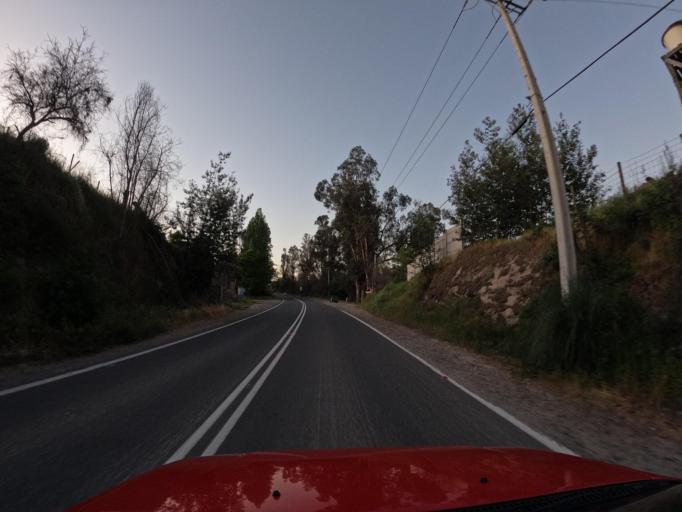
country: CL
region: O'Higgins
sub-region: Provincia de Cachapoal
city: San Vicente
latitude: -34.1633
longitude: -71.4091
